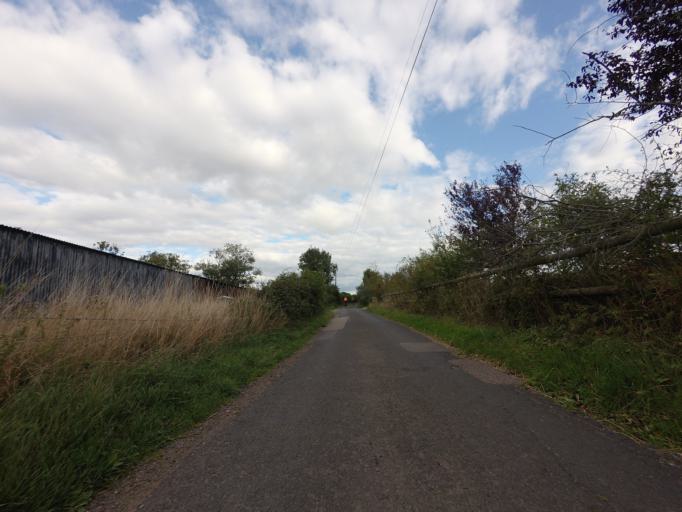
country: GB
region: England
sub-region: Kent
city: Staplehurst
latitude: 51.2075
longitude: 0.5369
